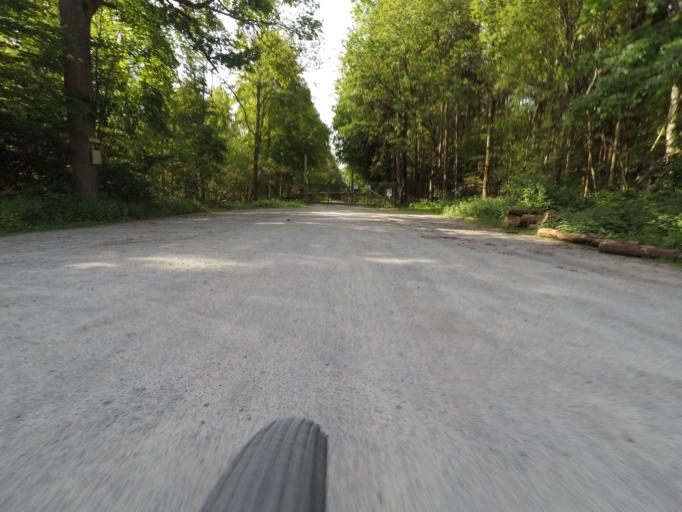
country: DE
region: Baden-Wuerttemberg
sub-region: Regierungsbezirk Stuttgart
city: Weil im Schonbuch
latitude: 48.6026
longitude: 9.0546
